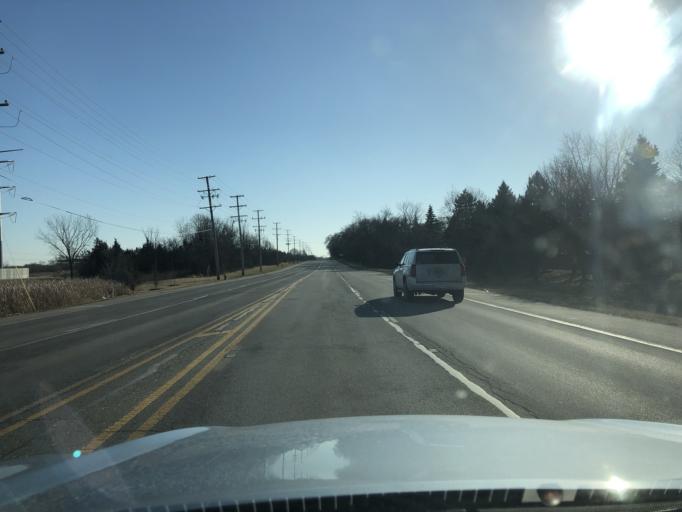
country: US
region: Illinois
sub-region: DuPage County
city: Itasca
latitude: 41.9792
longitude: -87.9982
